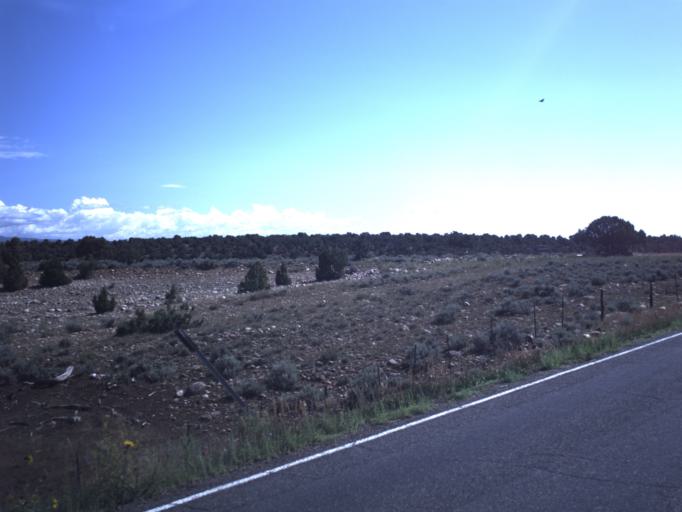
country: US
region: Utah
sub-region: Duchesne County
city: Duchesne
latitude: 40.3555
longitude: -110.3756
